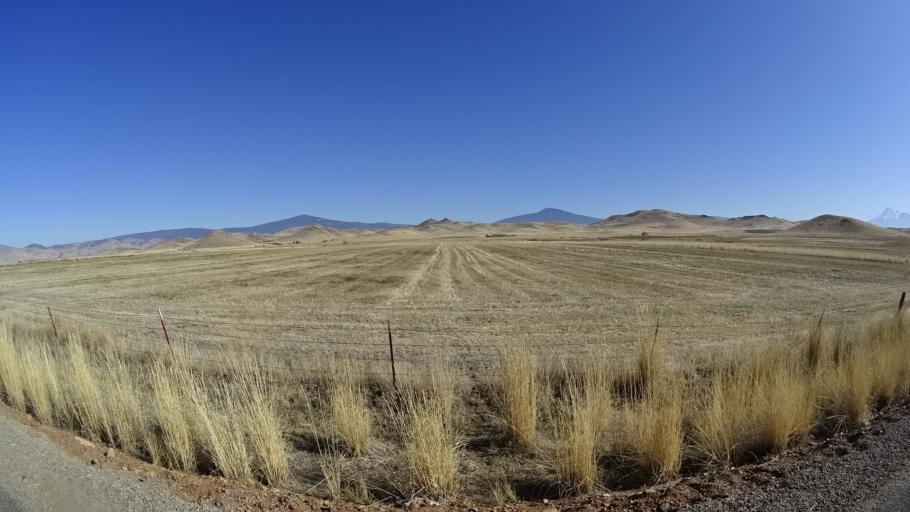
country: US
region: California
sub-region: Siskiyou County
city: Montague
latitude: 41.7618
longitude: -122.4570
